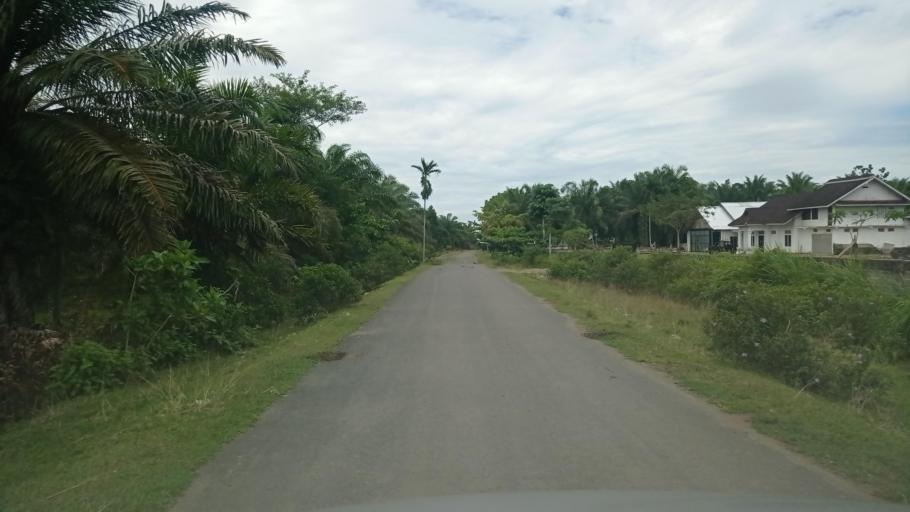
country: ID
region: Jambi
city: Sungai Penuh
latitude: -2.5257
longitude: 101.0829
